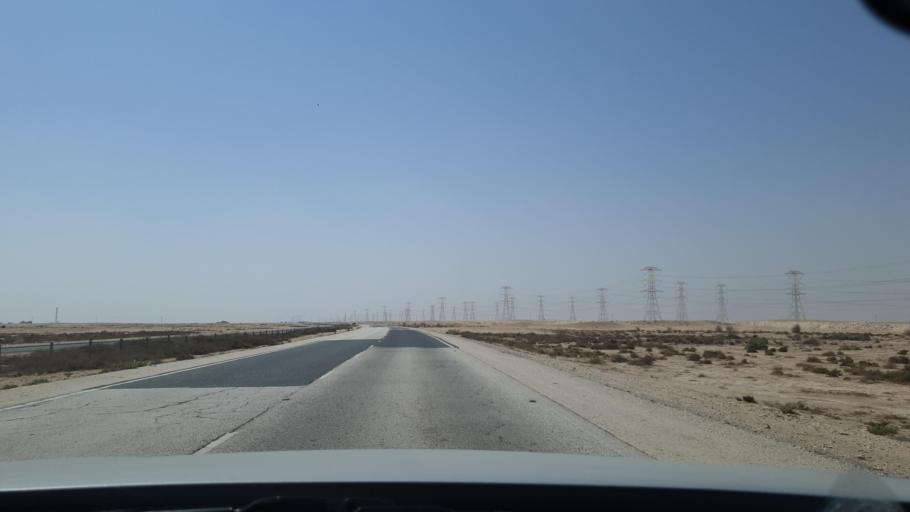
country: QA
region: Al Khawr
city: Al Khawr
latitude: 25.7444
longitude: 51.4633
